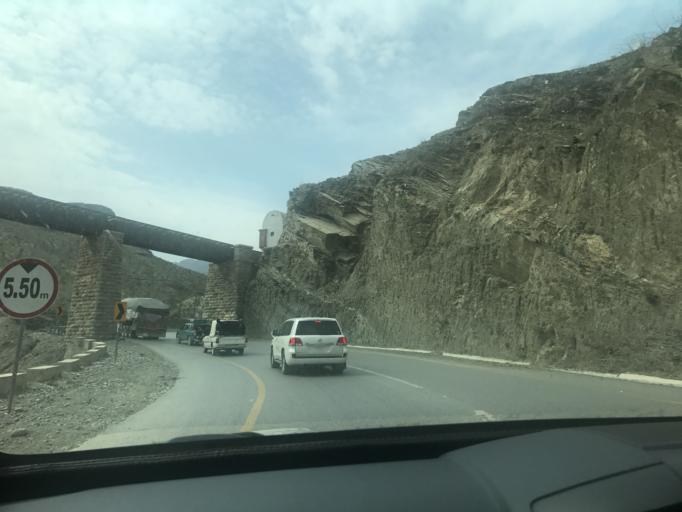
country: PK
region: Federally Administered Tribal Areas
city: Landi Kotal
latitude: 34.1051
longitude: 71.1310
